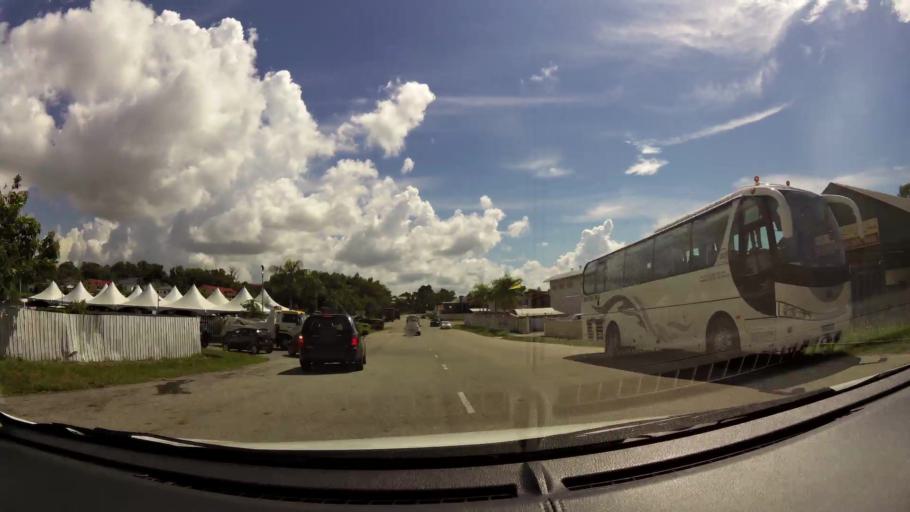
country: BN
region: Brunei and Muara
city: Bandar Seri Begawan
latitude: 4.9759
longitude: 114.9533
